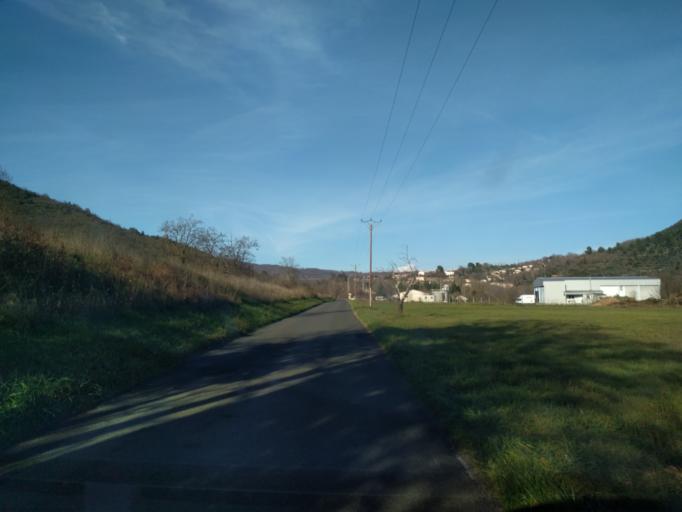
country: FR
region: Languedoc-Roussillon
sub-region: Departement de l'Aude
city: Quillan
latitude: 42.8876
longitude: 2.1909
